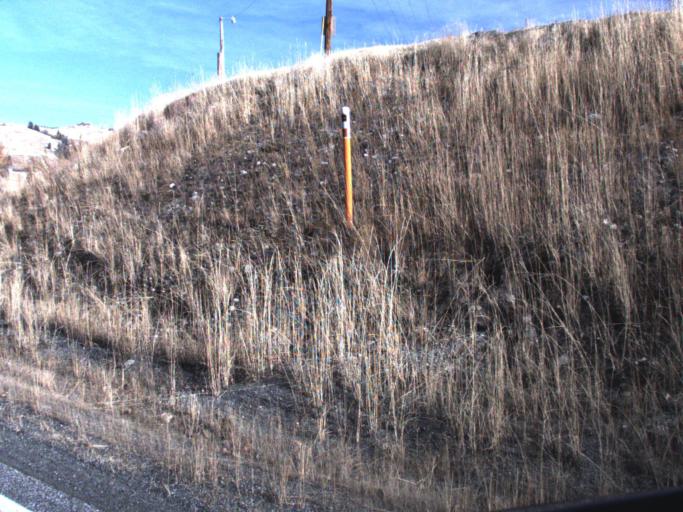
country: CA
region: British Columbia
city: Grand Forks
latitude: 48.8749
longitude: -118.6058
